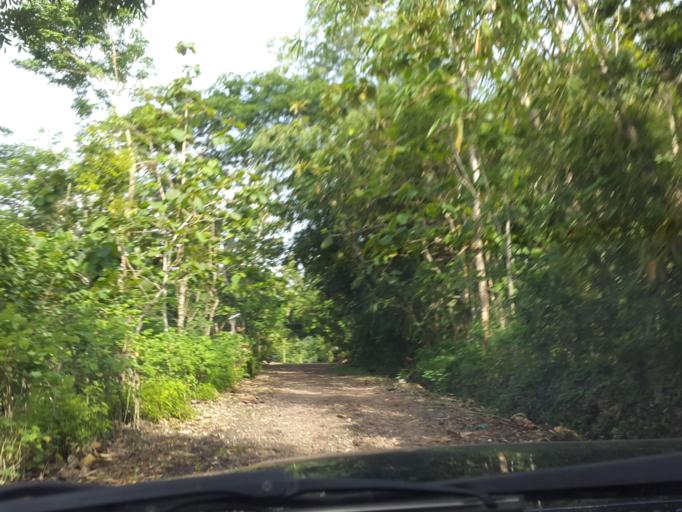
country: ID
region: Daerah Istimewa Yogyakarta
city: Wonosari
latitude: -7.9349
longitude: 110.6190
